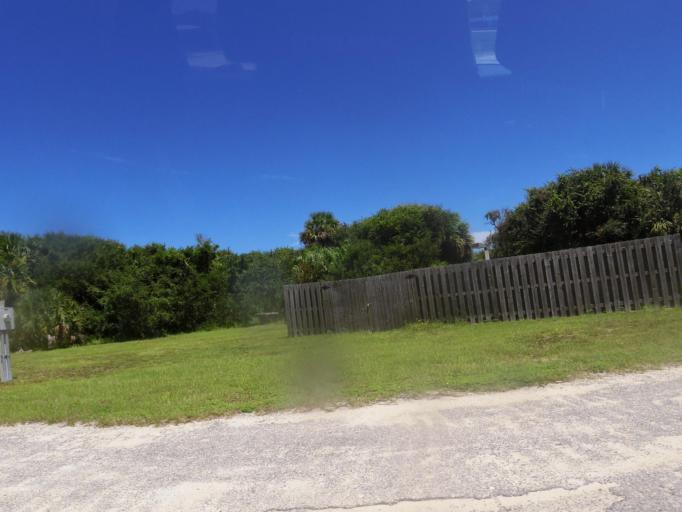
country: US
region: Florida
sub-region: Flagler County
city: Flagler Beach
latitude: 29.4374
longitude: -81.1098
